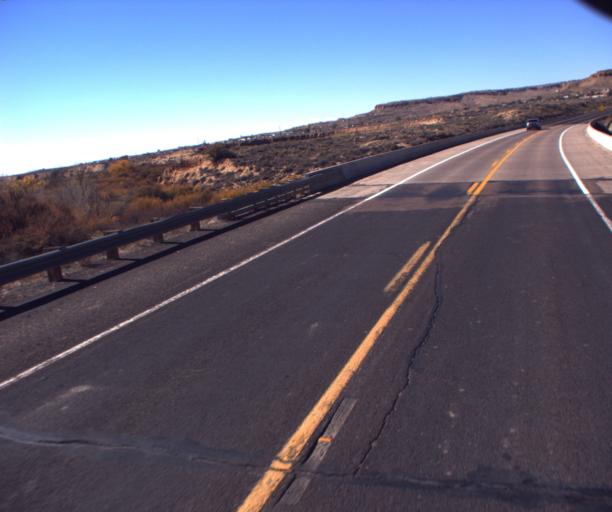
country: US
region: Arizona
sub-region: Navajo County
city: First Mesa
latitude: 35.8733
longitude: -110.6009
